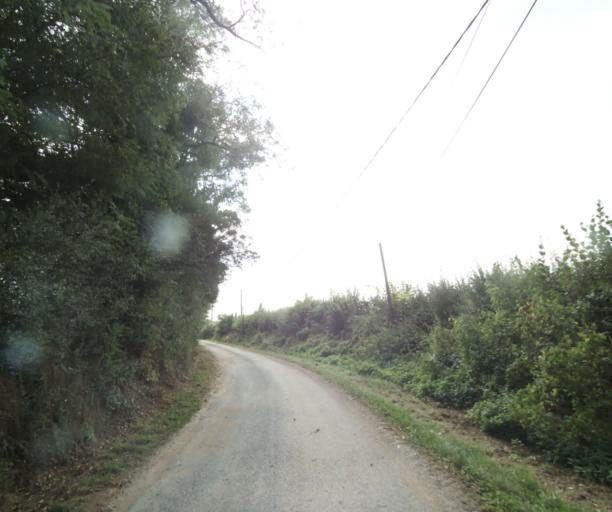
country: FR
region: Bourgogne
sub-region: Departement de Saone-et-Loire
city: Palinges
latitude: 46.5005
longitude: 4.2367
